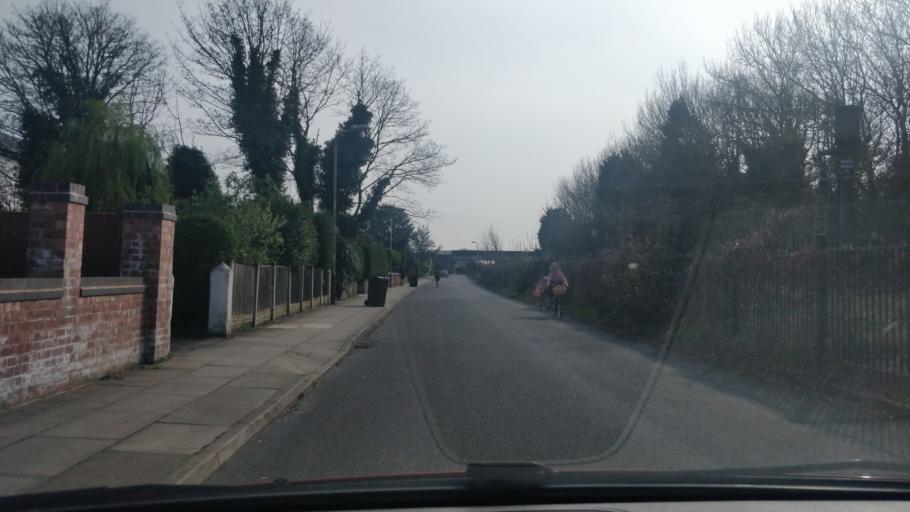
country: GB
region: England
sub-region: Sefton
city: Formby
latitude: 53.6007
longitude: -3.0435
